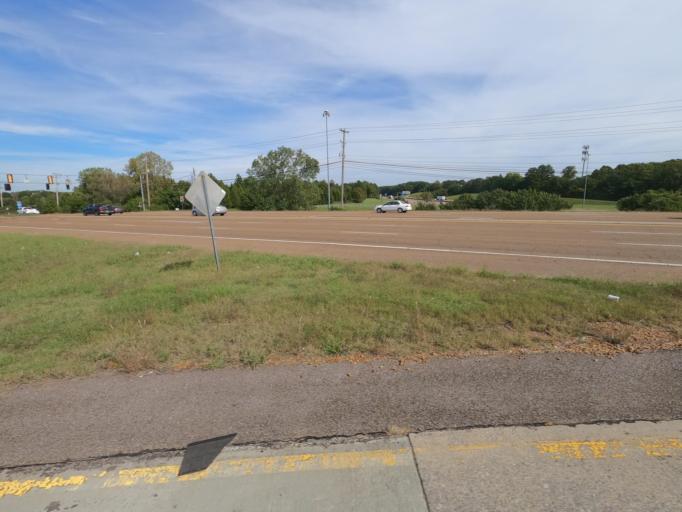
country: US
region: Tennessee
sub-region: Shelby County
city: Lakeland
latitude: 35.1958
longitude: -89.7927
